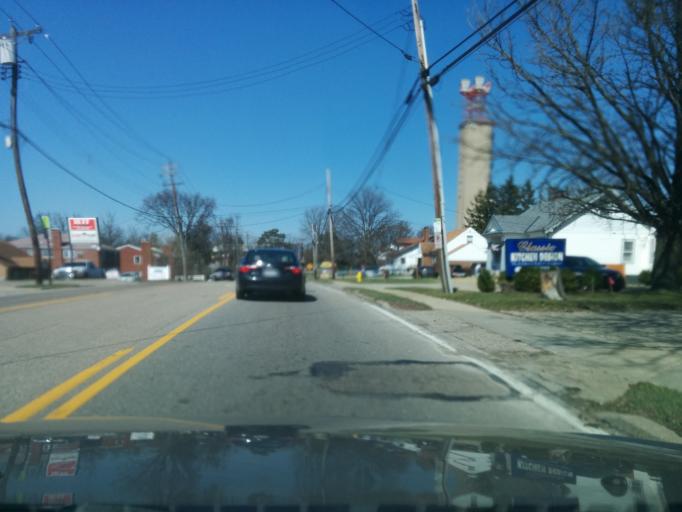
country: US
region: Ohio
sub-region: Hamilton County
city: Monfort Heights
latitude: 39.1960
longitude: -84.5999
